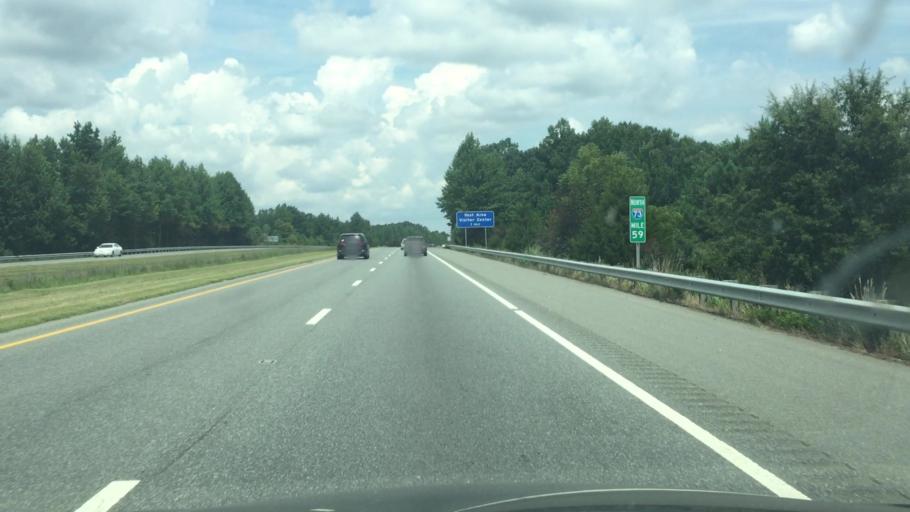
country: US
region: North Carolina
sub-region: Montgomery County
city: Biscoe
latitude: 35.4980
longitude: -79.7807
